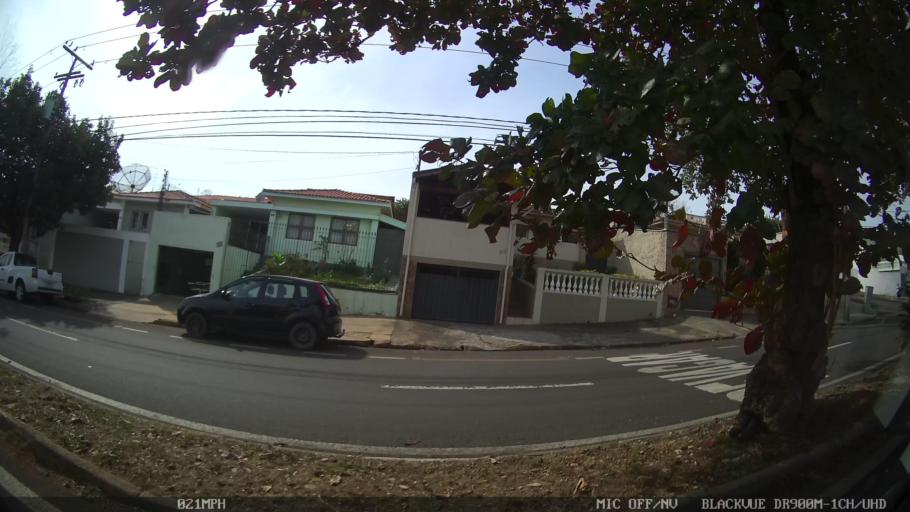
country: BR
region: Sao Paulo
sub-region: Piracicaba
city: Piracicaba
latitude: -22.7327
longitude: -47.6679
